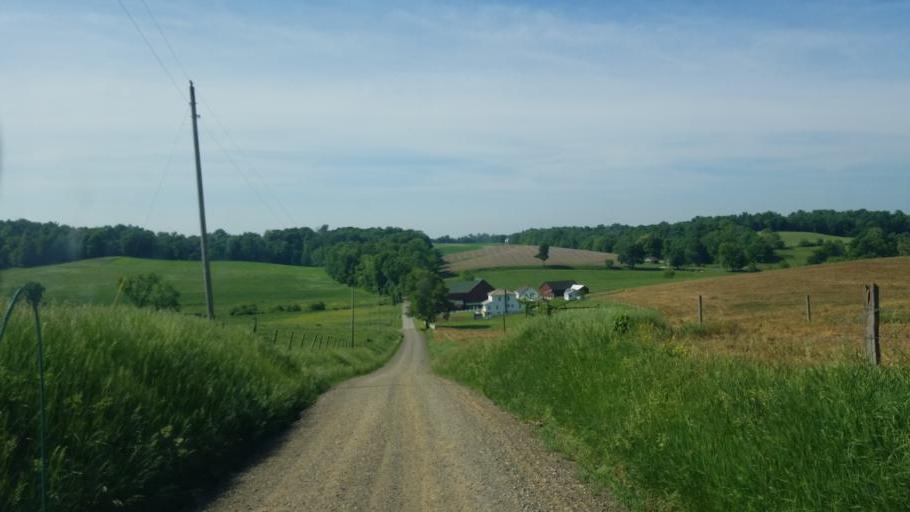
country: US
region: Ohio
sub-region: Tuscarawas County
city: Sugarcreek
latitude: 40.4681
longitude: -81.7564
